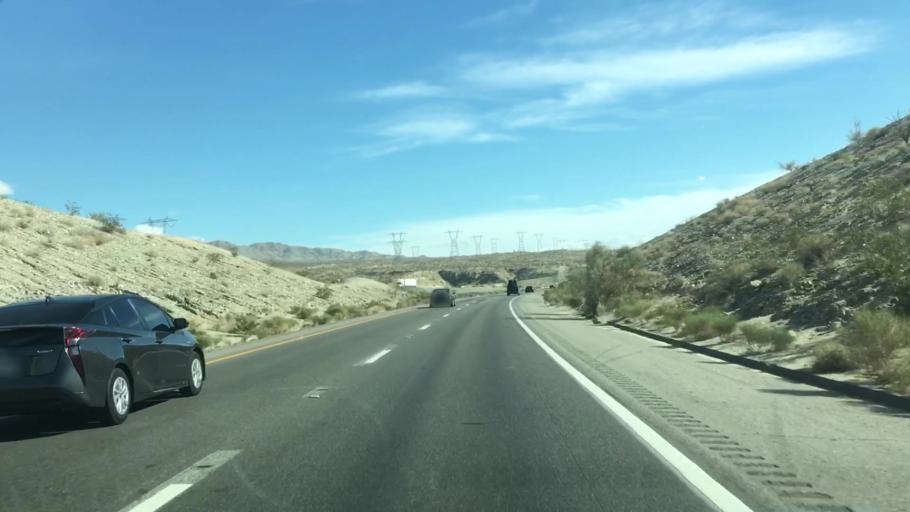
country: US
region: California
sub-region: Riverside County
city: Thermal
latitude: 33.6993
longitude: -116.0670
